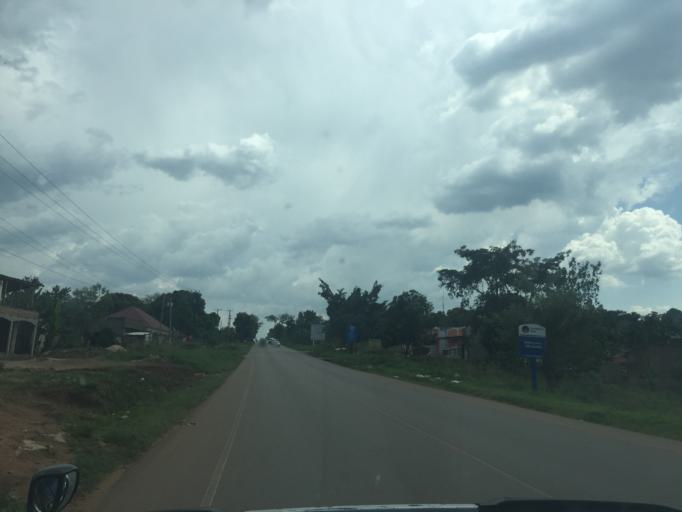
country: UG
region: Central Region
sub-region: Luwero District
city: Wobulenzi
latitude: 0.6983
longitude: 32.5226
